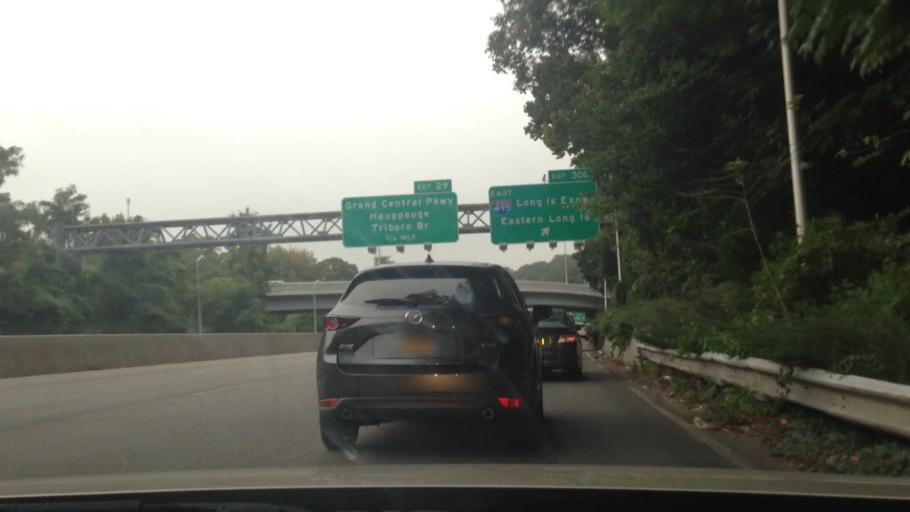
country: US
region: New York
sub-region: Nassau County
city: University Gardens
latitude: 40.7556
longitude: -73.7461
